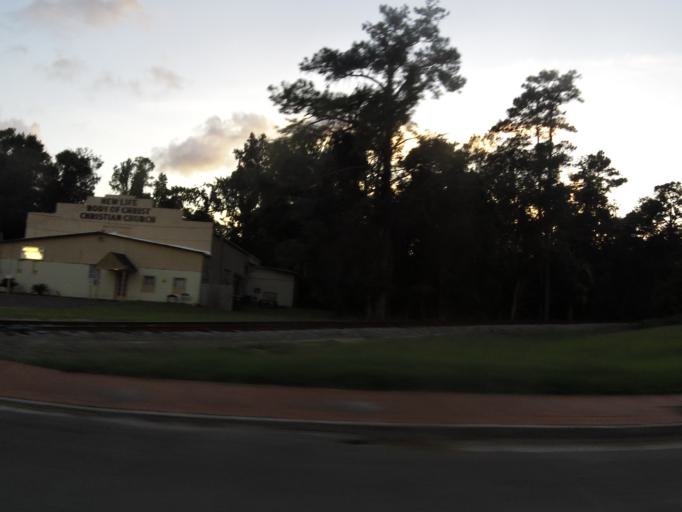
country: US
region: Georgia
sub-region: Camden County
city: Kingsland
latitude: 30.7969
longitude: -81.6896
